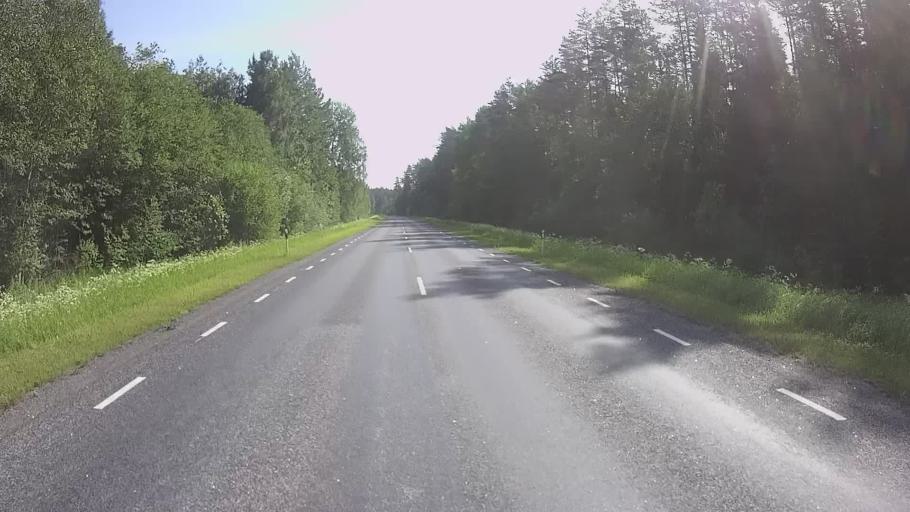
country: EE
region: Valgamaa
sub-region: Torva linn
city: Torva
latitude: 58.0569
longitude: 26.0080
